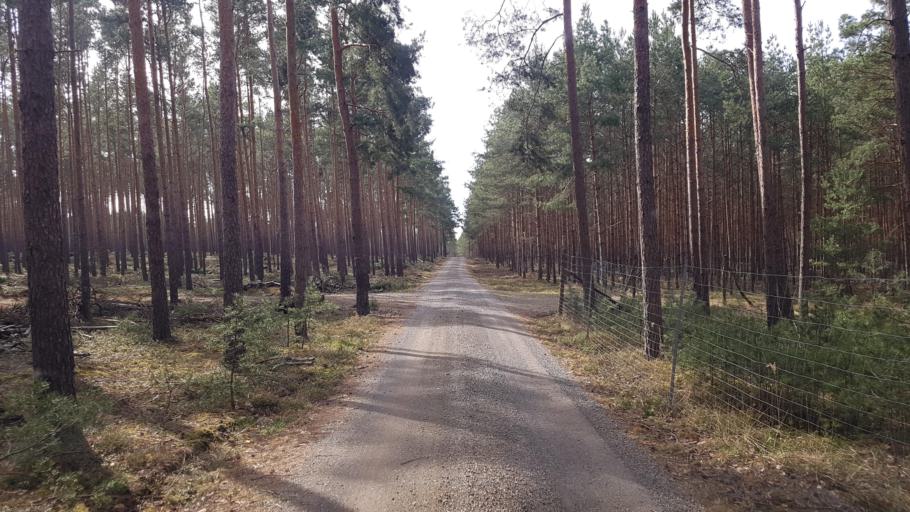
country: DE
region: Brandenburg
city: Elsterwerda
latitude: 51.4938
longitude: 13.4598
